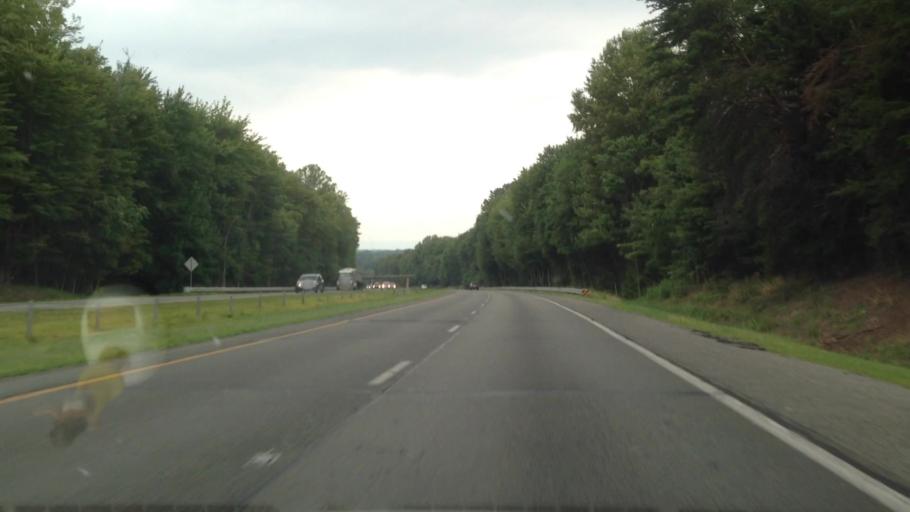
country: US
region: North Carolina
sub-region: Surry County
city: Pilot Mountain
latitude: 36.3544
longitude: -80.4705
